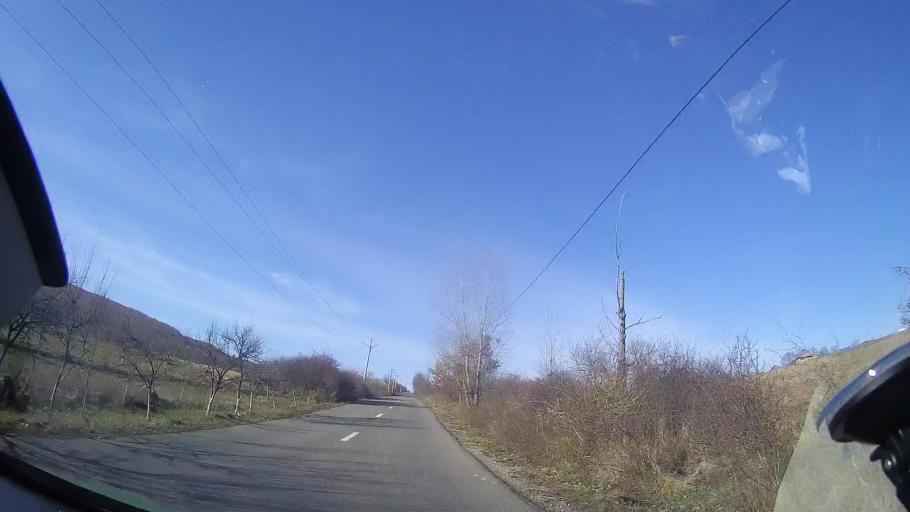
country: RO
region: Bihor
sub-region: Comuna Vadu Crisului
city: Vadu Crisului
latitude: 46.9720
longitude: 22.5449
